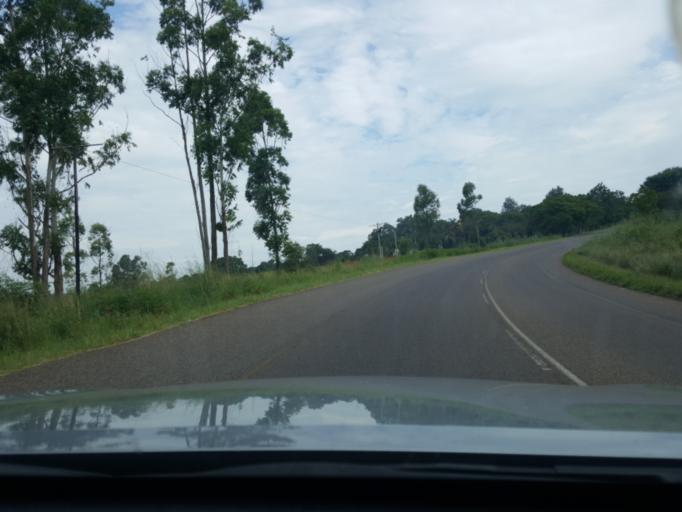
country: ZA
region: Mpumalanga
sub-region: Ehlanzeni District
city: White River
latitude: -25.3364
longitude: 31.0258
